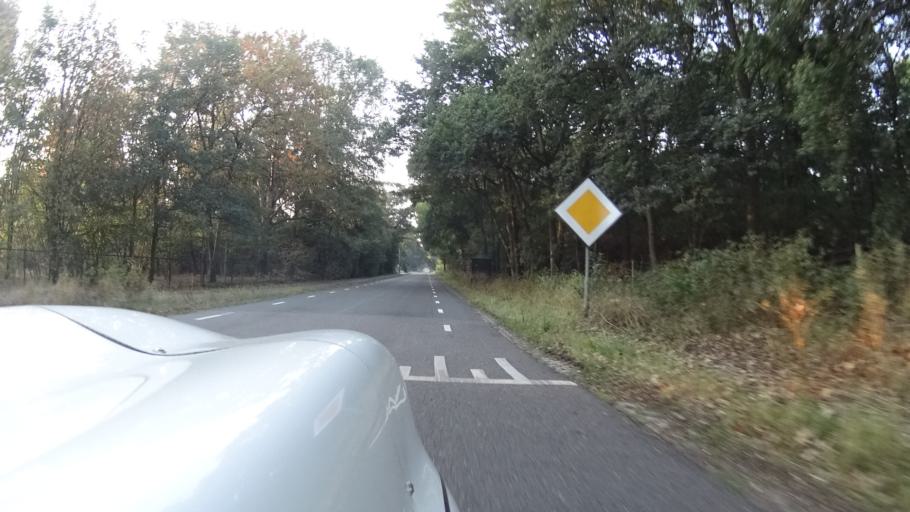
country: NL
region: North Brabant
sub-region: Gemeente Boxmeer
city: Overloon
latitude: 51.5921
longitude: 5.9265
